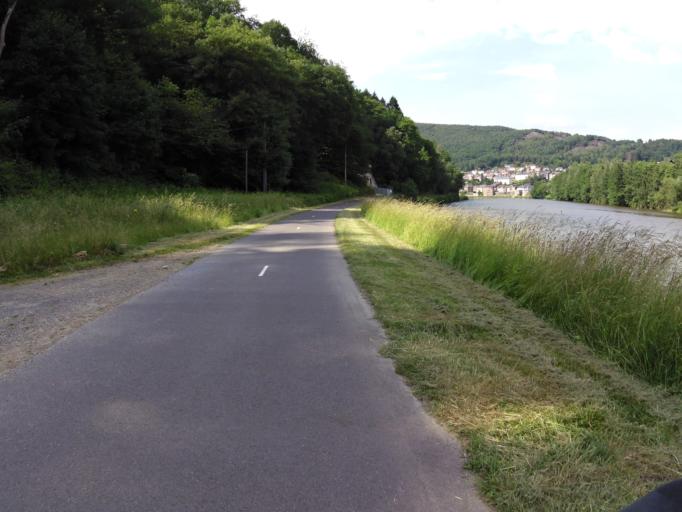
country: FR
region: Champagne-Ardenne
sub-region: Departement des Ardennes
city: Montherme
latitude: 49.8798
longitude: 4.7375
